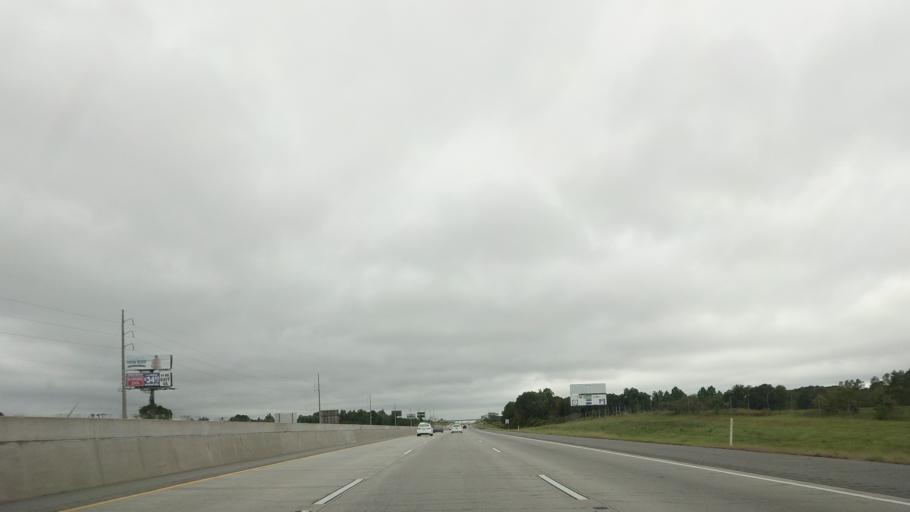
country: US
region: Georgia
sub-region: Tift County
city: Unionville
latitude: 31.4099
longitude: -83.5033
